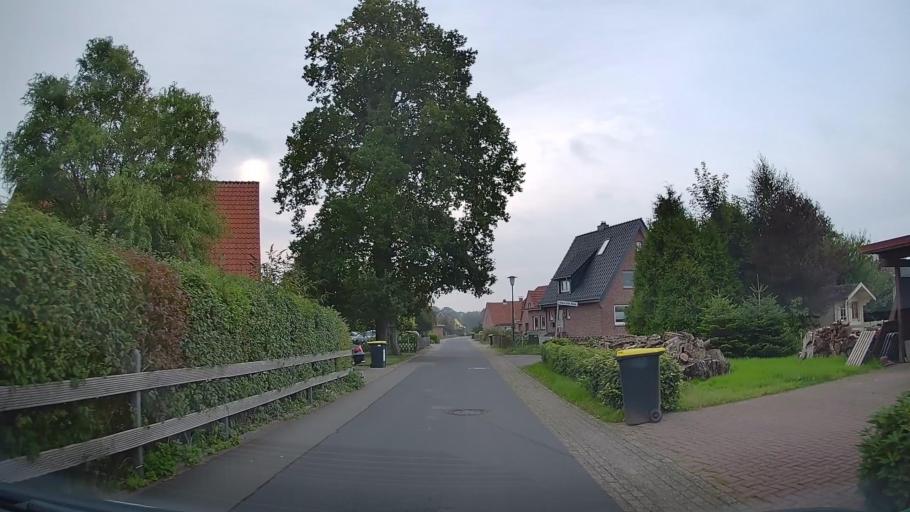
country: DE
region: Lower Saxony
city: Wanna
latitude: 53.8284
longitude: 8.7660
